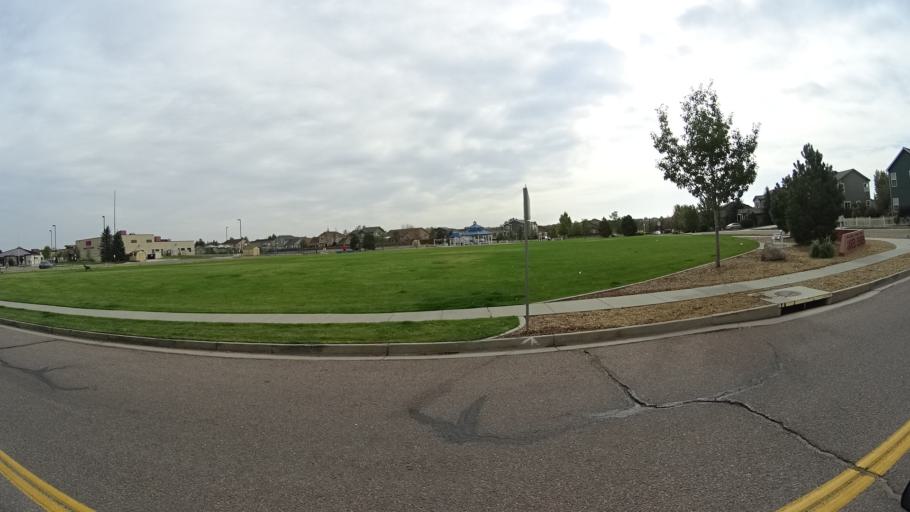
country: US
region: Colorado
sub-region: El Paso County
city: Cimarron Hills
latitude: 38.9204
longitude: -104.7012
